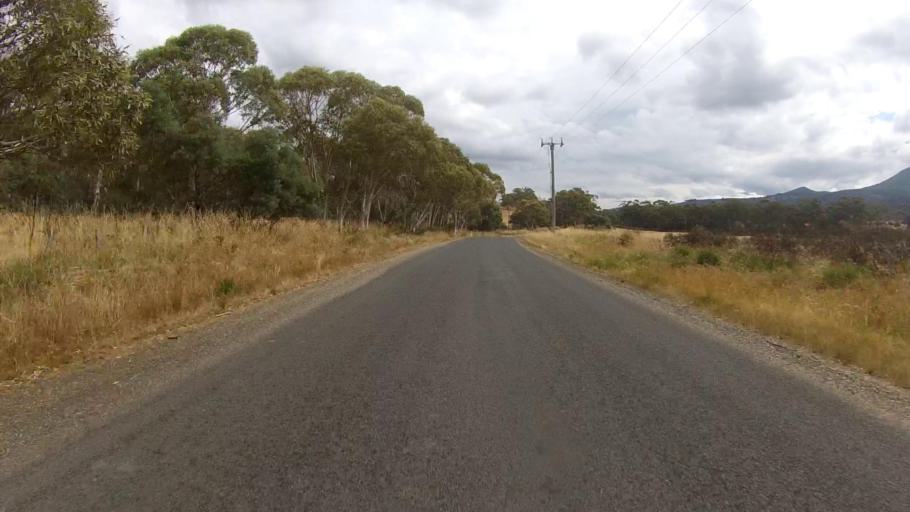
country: AU
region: Tasmania
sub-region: Break O'Day
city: St Helens
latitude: -41.8221
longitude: 147.9067
